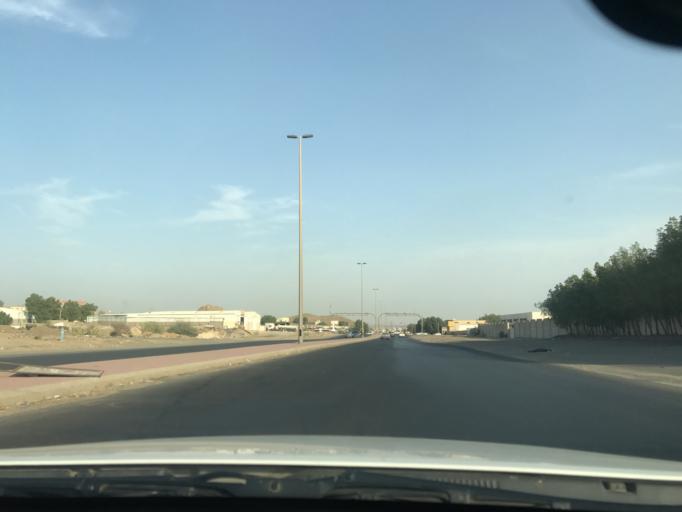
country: SA
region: Makkah
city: Jeddah
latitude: 21.4083
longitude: 39.4260
